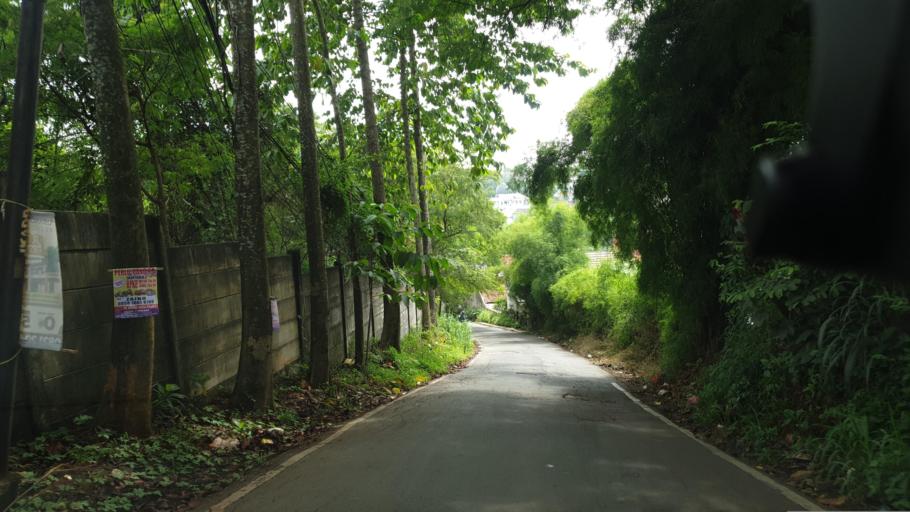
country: ID
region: West Java
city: Pamulang
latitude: -6.3481
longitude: 106.7721
